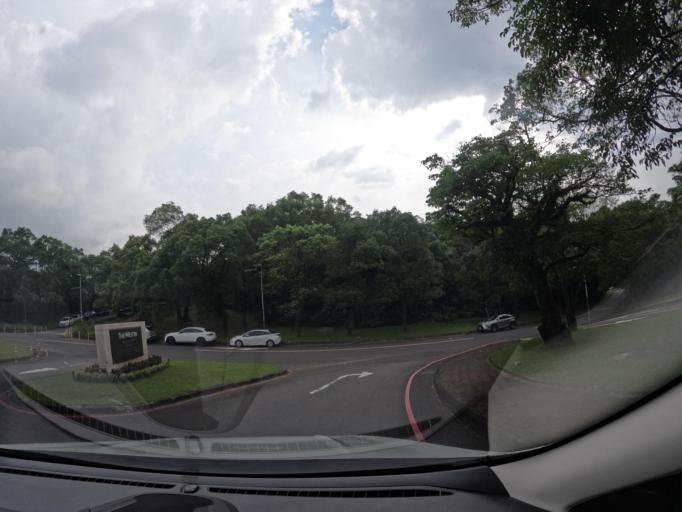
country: TW
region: Taiwan
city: Daxi
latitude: 24.8817
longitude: 121.3255
